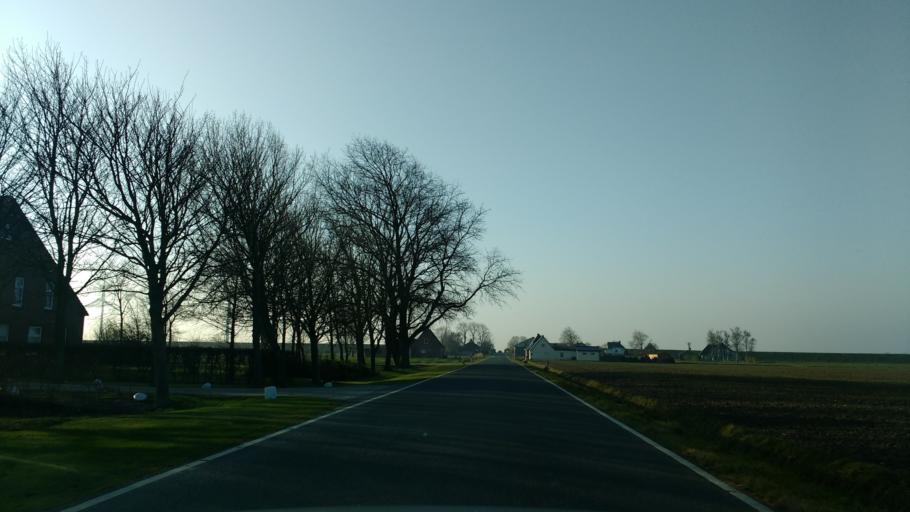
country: DE
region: Schleswig-Holstein
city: Friedrichskoog
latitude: 53.9886
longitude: 8.9309
